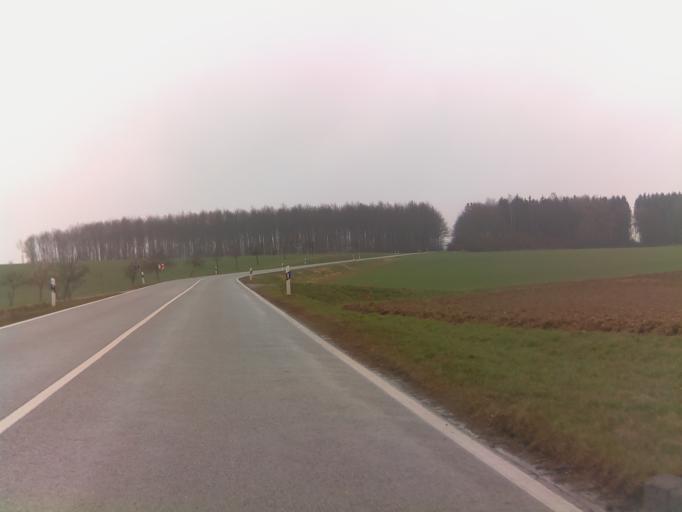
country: DE
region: Rheinland-Pfalz
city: Mengerschied
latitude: 49.9187
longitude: 7.5142
